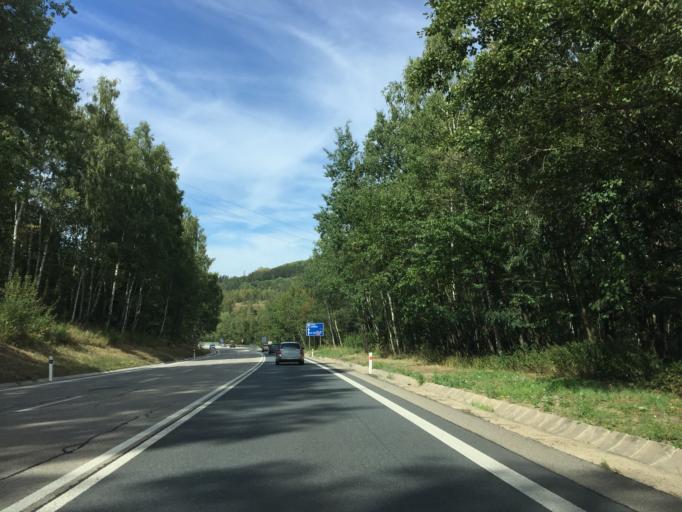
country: CZ
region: Central Bohemia
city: Votice
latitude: 49.6340
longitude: 14.6514
